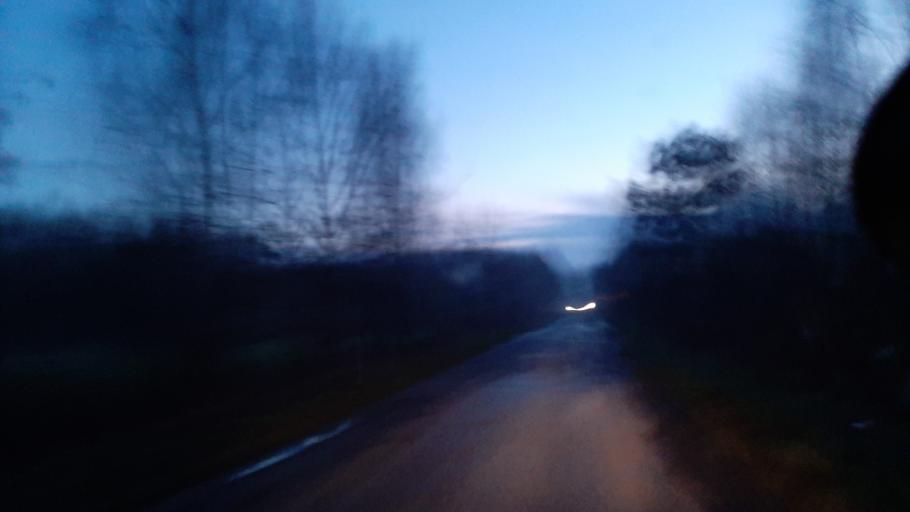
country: PL
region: Lublin Voivodeship
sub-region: Powiat lubartowski
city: Firlej
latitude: 51.5278
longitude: 22.5017
